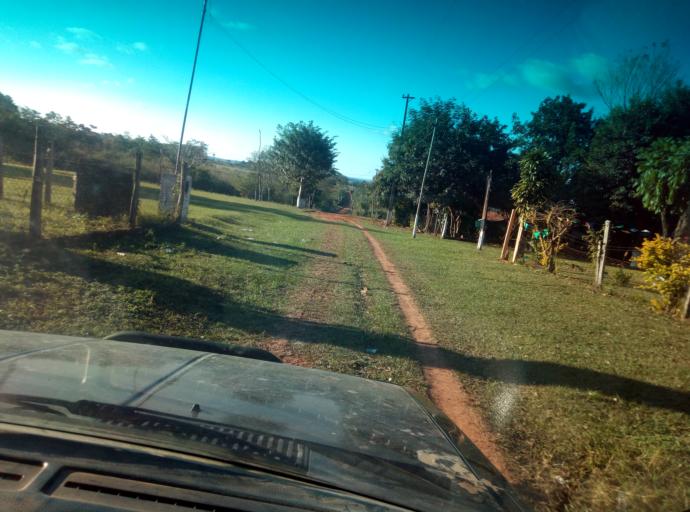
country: PY
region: Caaguazu
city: Carayao
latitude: -25.1812
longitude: -56.2647
